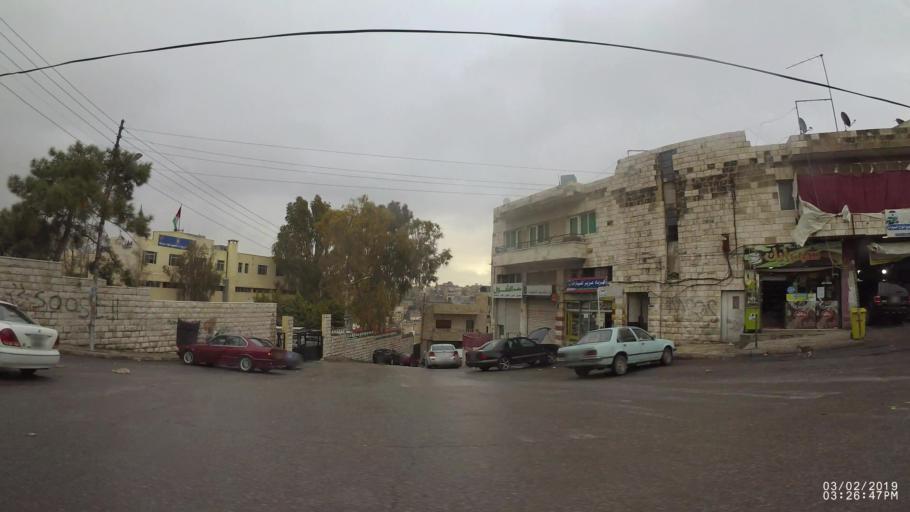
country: JO
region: Amman
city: Amman
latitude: 31.9605
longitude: 35.9317
